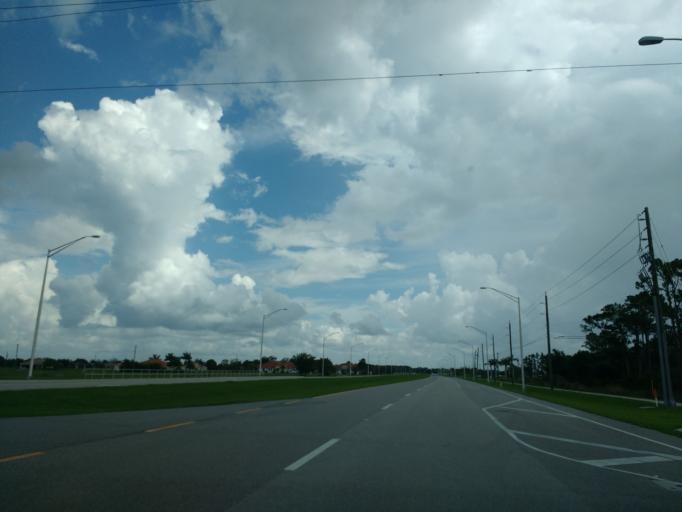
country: US
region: Florida
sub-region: Lee County
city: Burnt Store Marina
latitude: 26.7868
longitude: -82.0379
